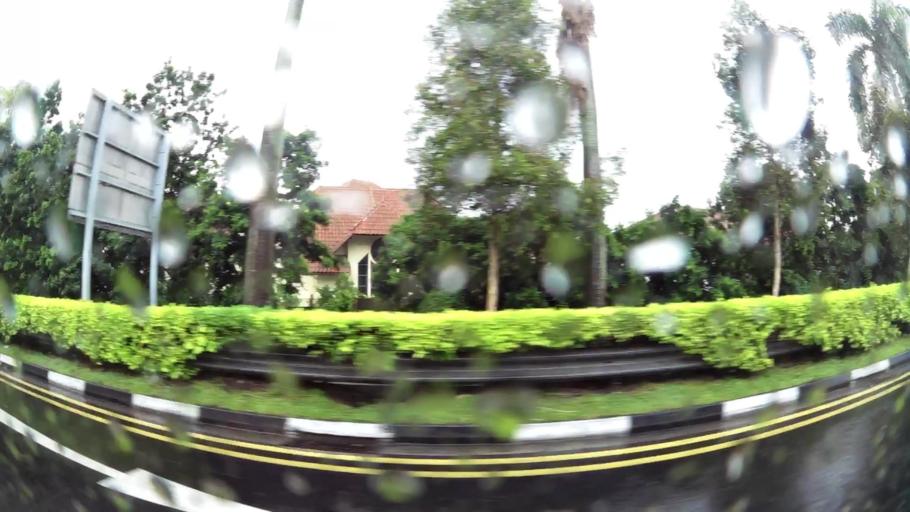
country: SG
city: Singapore
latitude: 1.3212
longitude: 103.9184
